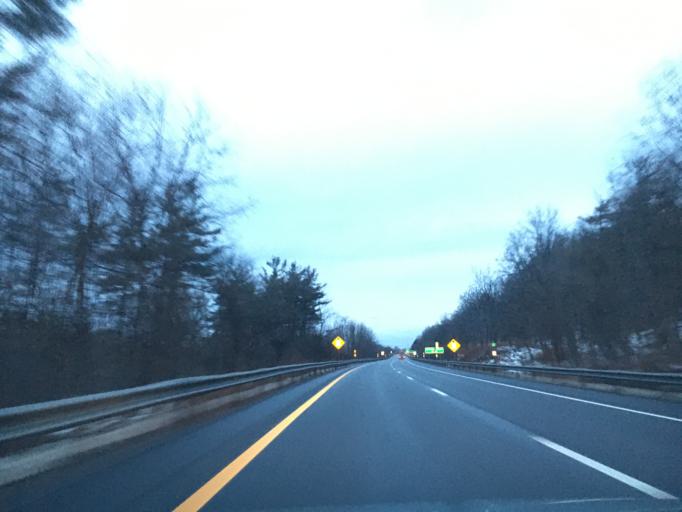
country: US
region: New York
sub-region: Onondaga County
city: Nedrow
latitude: 42.9900
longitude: -76.1340
